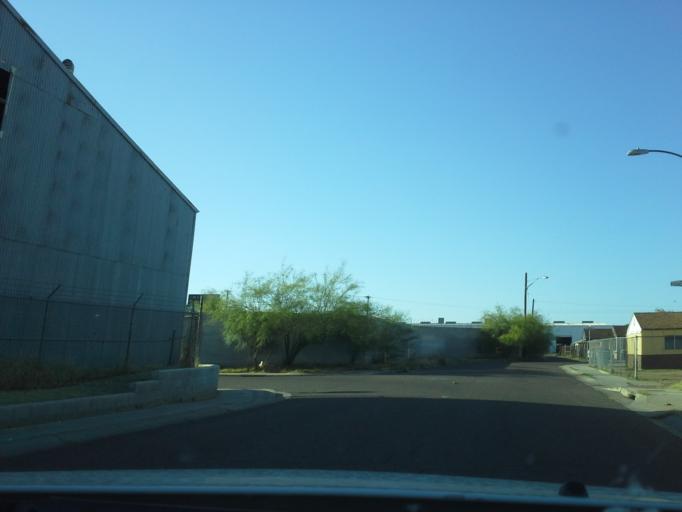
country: US
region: Arizona
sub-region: Maricopa County
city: Phoenix
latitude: 33.4317
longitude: -112.0989
